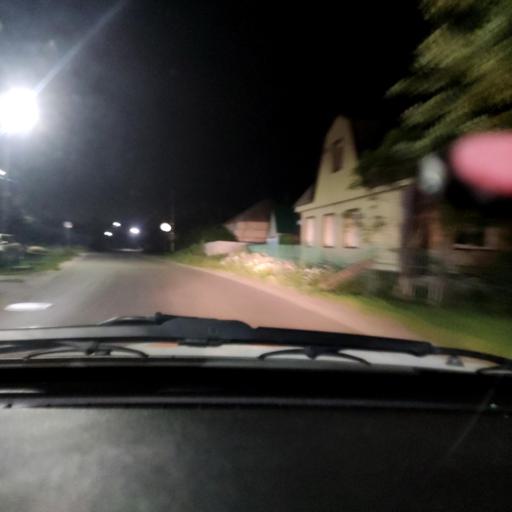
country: RU
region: Voronezj
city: Novaya Usman'
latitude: 51.6373
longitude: 39.4234
